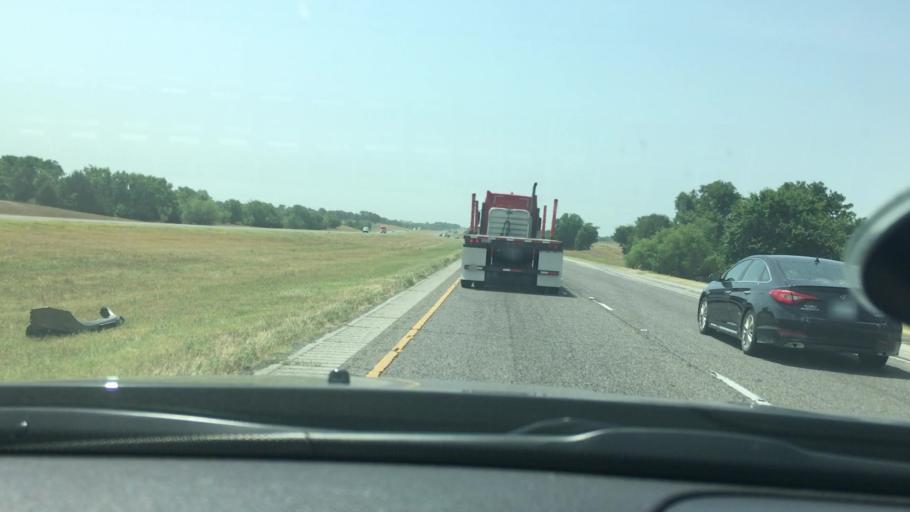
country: US
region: Oklahoma
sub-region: Garvin County
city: Wynnewood
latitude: 34.5979
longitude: -97.2098
